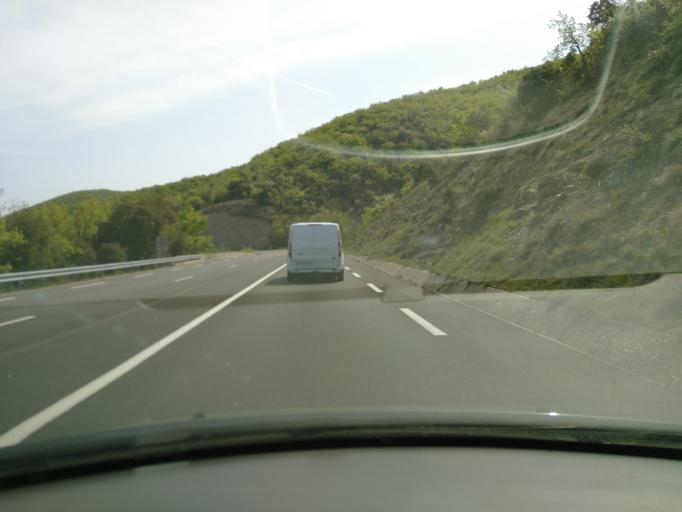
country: FR
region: Rhone-Alpes
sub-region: Departement de l'Ardeche
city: Alba-la-Romaine
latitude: 44.5693
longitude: 4.6342
